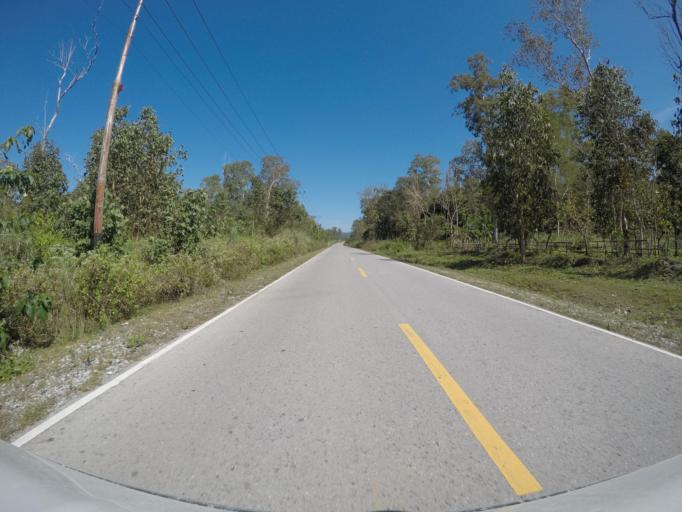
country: TL
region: Viqueque
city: Viqueque
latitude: -8.9699
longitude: 126.0295
